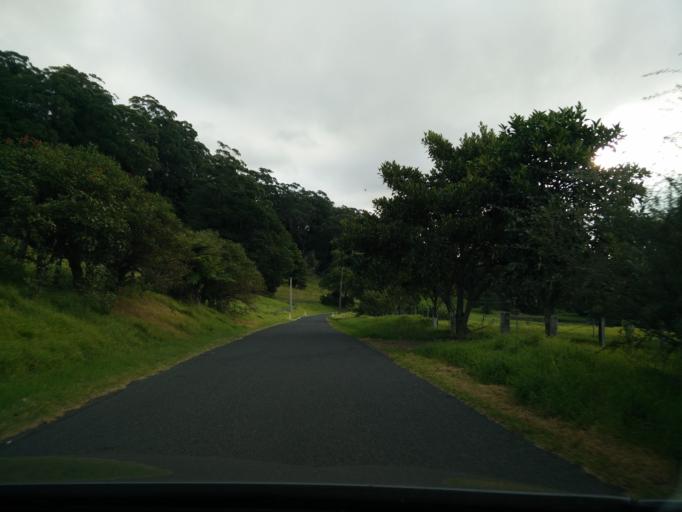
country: AU
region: New South Wales
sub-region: Kiama
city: Jamberoo
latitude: -34.6932
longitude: 150.7902
